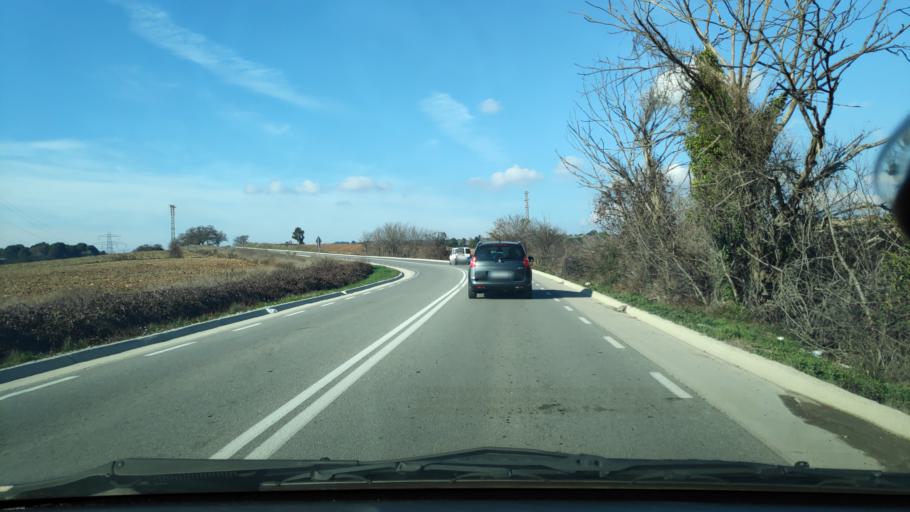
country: ES
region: Catalonia
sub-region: Provincia de Barcelona
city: Sant Cugat del Valles
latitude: 41.4818
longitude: 2.1014
